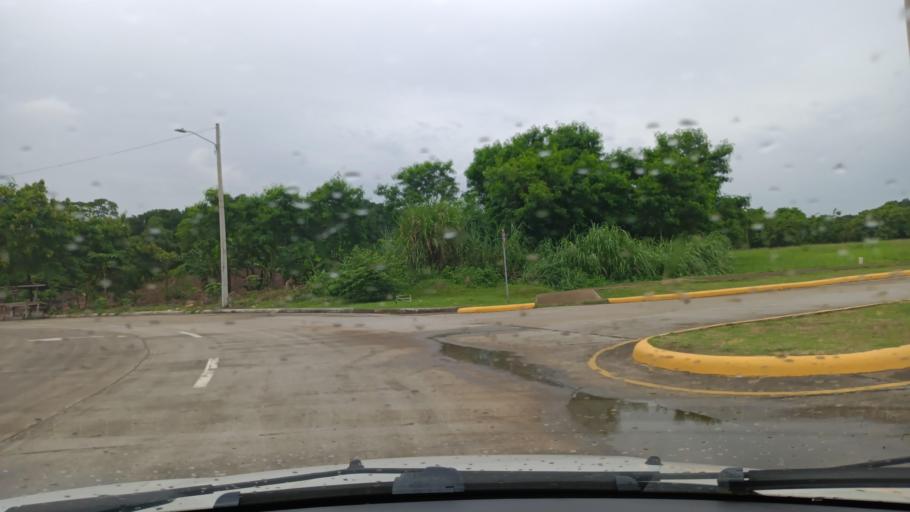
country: PA
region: Panama
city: Tocumen
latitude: 9.0374
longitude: -79.4048
